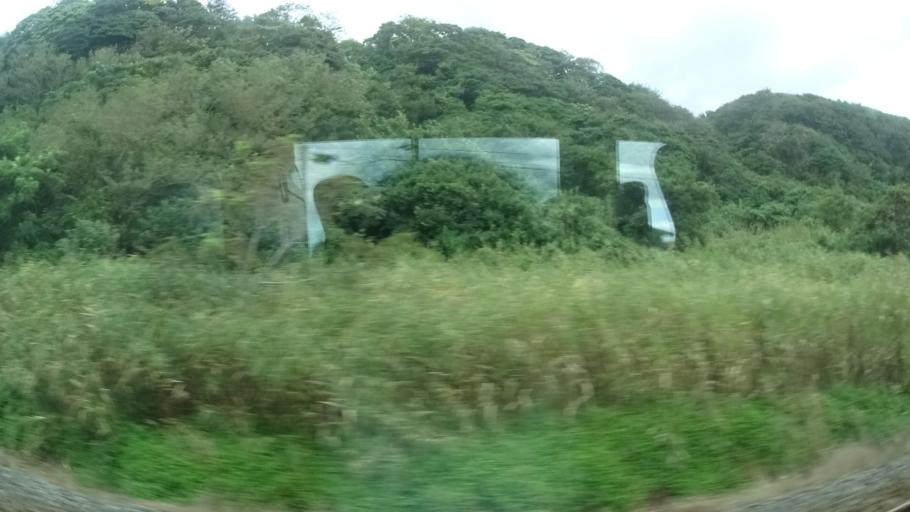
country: JP
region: Niigata
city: Murakami
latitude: 38.2637
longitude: 139.4473
